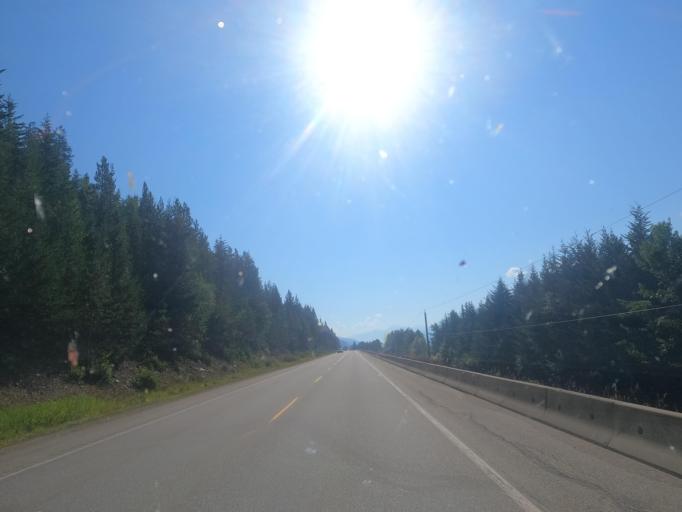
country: CA
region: Alberta
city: Jasper Park Lodge
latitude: 52.9593
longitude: -118.9028
